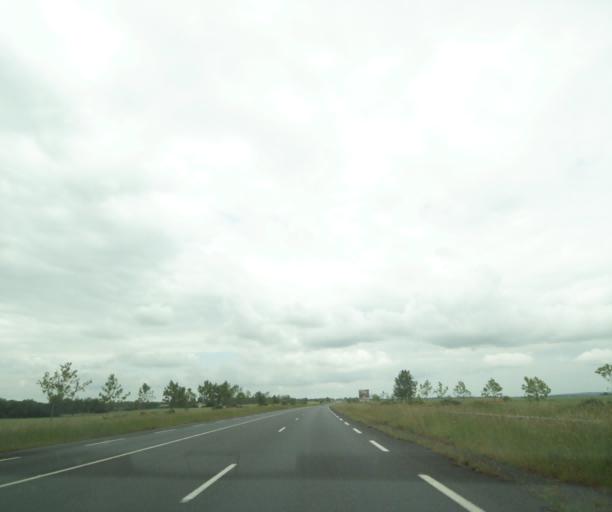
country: FR
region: Poitou-Charentes
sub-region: Departement des Deux-Sevres
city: Saint-Varent
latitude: 46.8929
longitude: -0.1934
